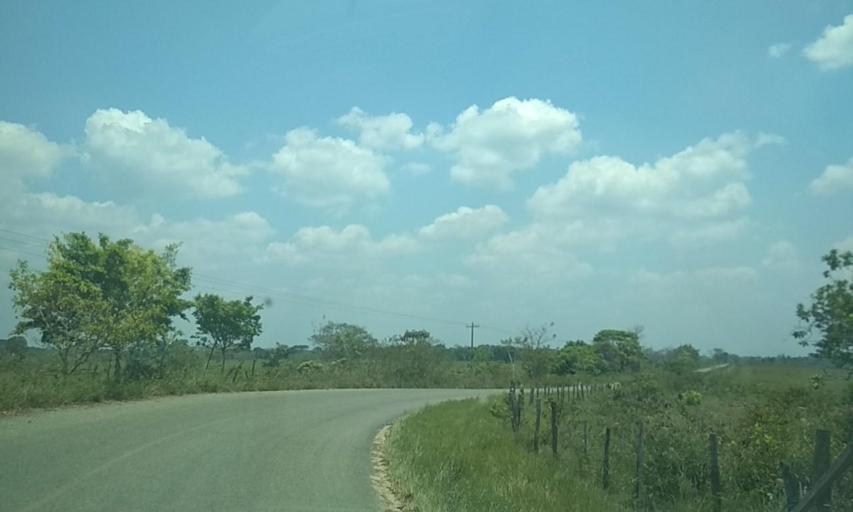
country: MX
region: Tabasco
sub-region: Huimanguillo
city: Francisco Rueda
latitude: 17.8308
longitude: -93.8729
